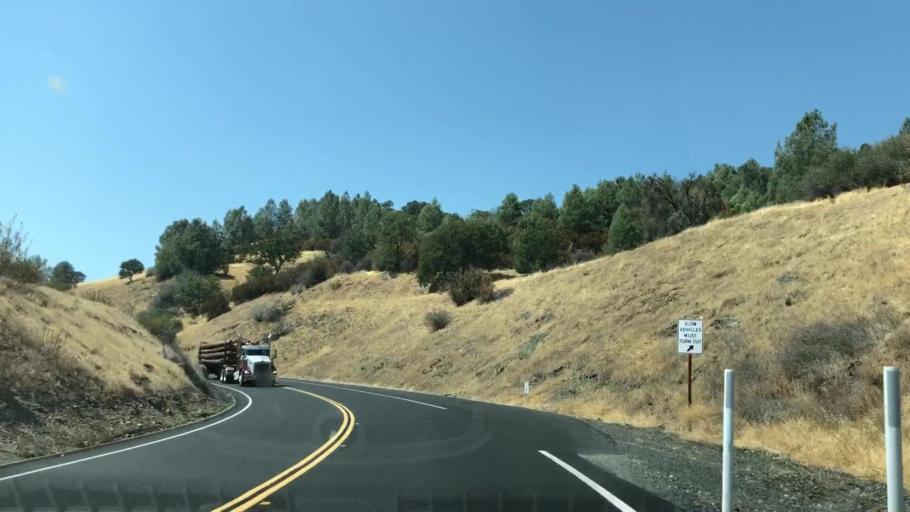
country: US
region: California
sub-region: Tuolumne County
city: Tuolumne City
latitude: 37.8176
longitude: -120.3008
